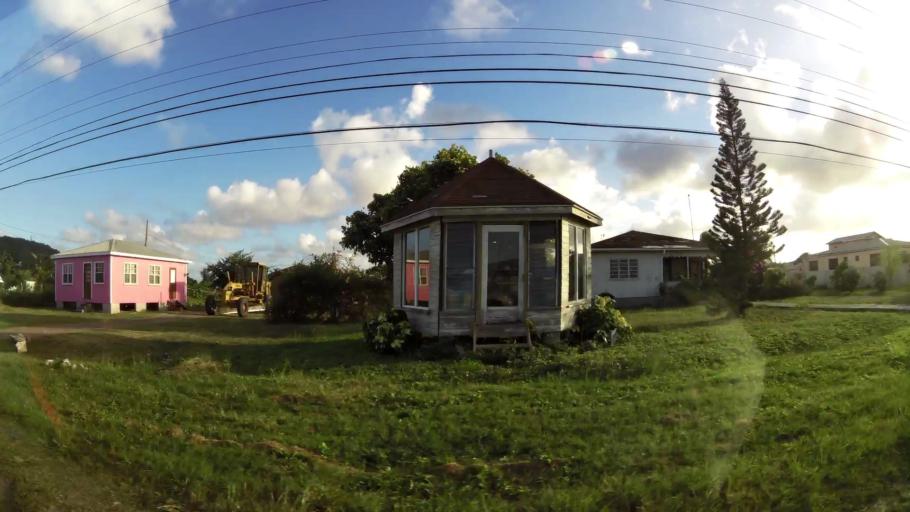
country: AG
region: Saint George
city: Piggotts
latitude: 17.1268
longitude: -61.8087
